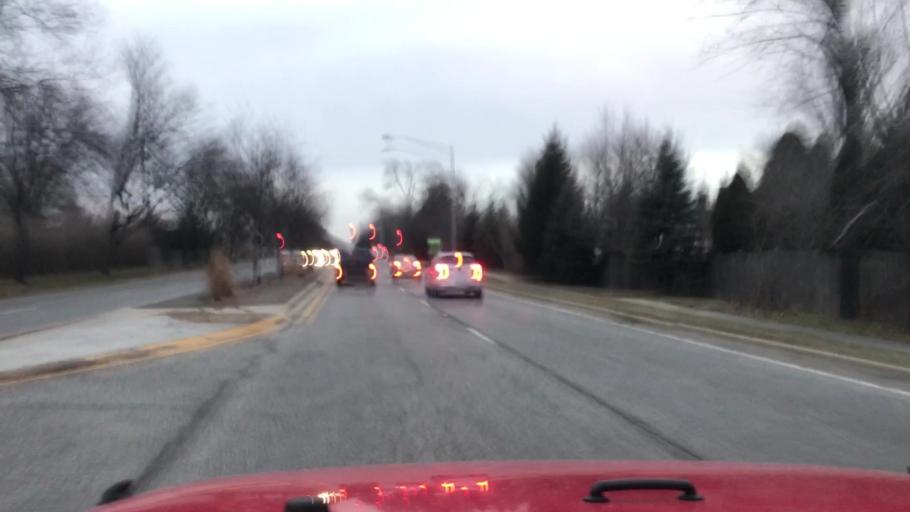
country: US
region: Illinois
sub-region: Cook County
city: Arlington Heights
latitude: 42.1229
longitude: -87.9801
